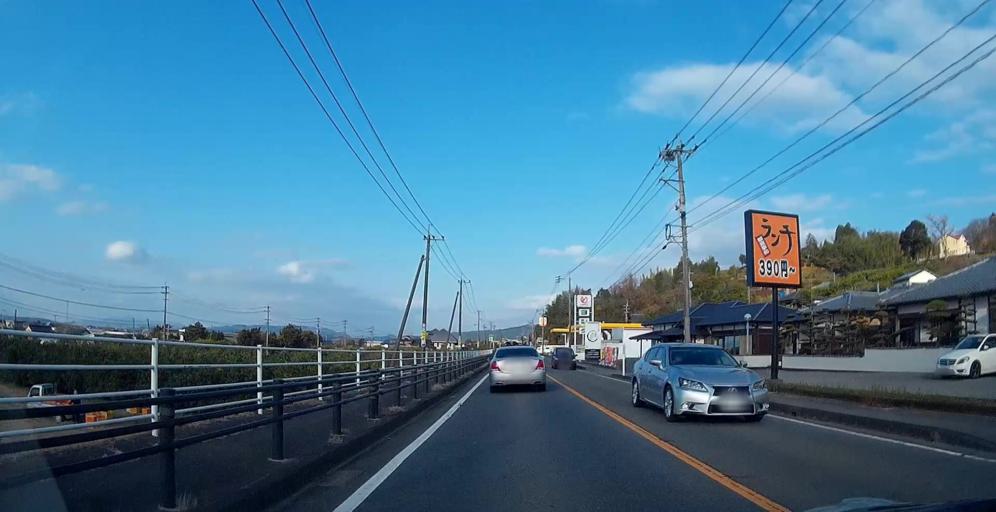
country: JP
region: Kumamoto
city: Matsubase
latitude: 32.5742
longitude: 130.6935
